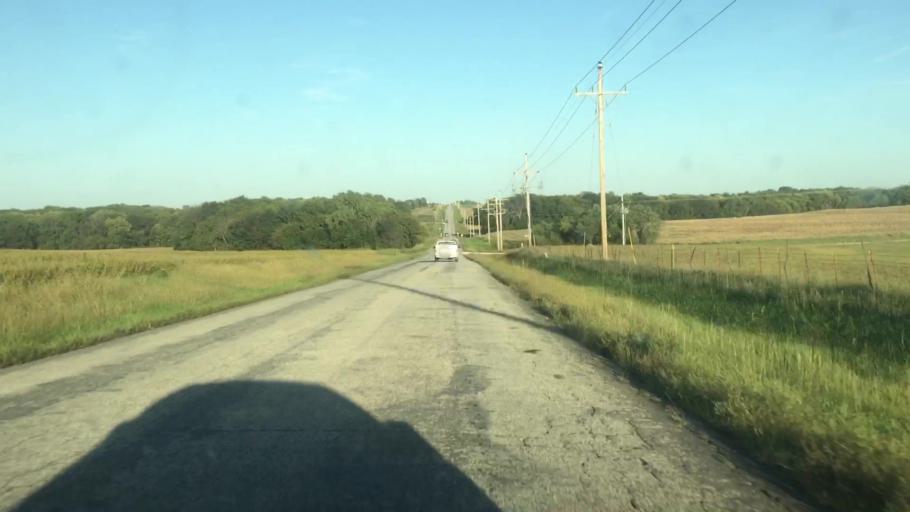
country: US
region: Kansas
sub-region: Brown County
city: Horton
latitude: 39.5656
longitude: -95.3850
